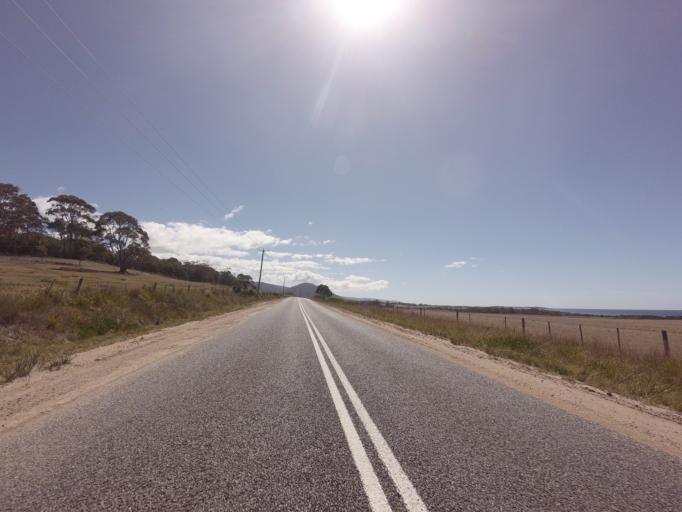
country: AU
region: Tasmania
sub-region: Break O'Day
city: St Helens
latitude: -41.7907
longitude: 148.2623
